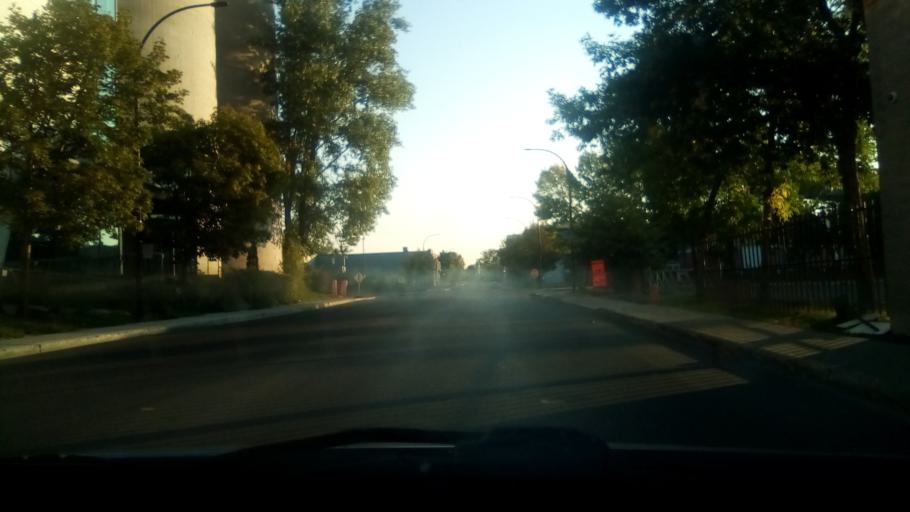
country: CA
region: Quebec
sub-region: Montreal
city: Montreal
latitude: 45.4866
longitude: -73.5613
